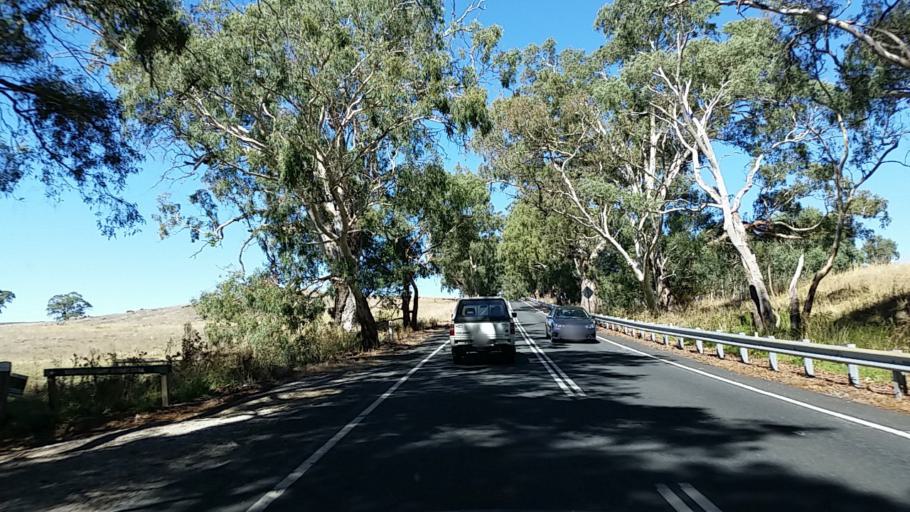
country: AU
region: South Australia
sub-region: Adelaide Hills
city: Birdwood
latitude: -34.7532
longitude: 138.9977
